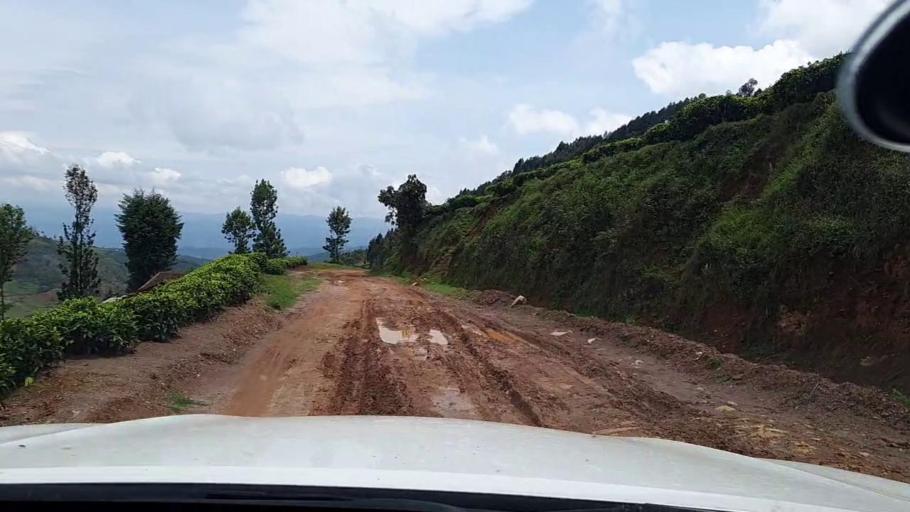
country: RW
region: Western Province
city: Kibuye
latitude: -2.1693
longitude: 29.3974
